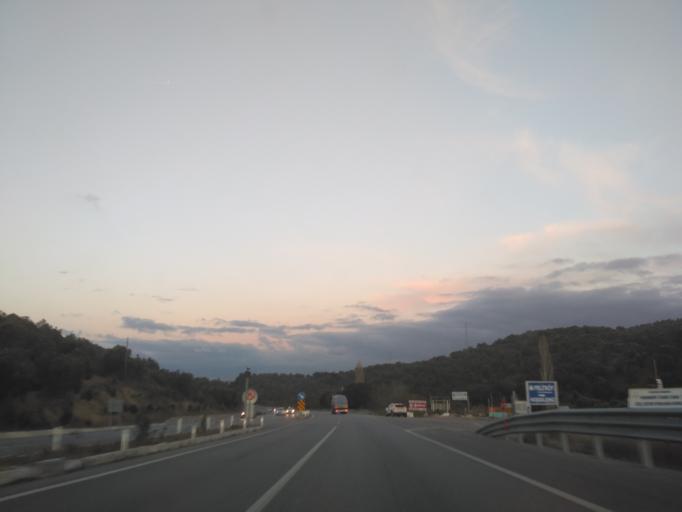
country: TR
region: Balikesir
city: Burhaniye
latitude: 39.4635
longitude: 26.9028
